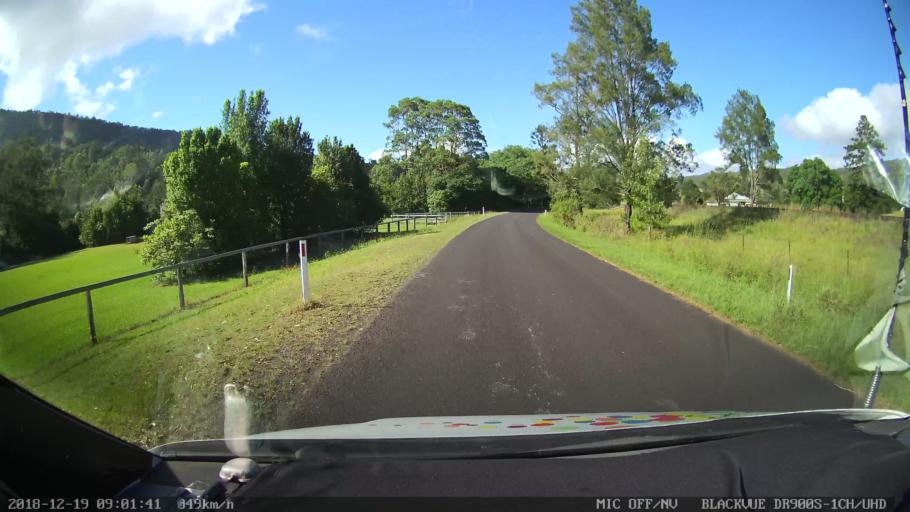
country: AU
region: New South Wales
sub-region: Kyogle
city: Kyogle
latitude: -28.4407
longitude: 152.9590
